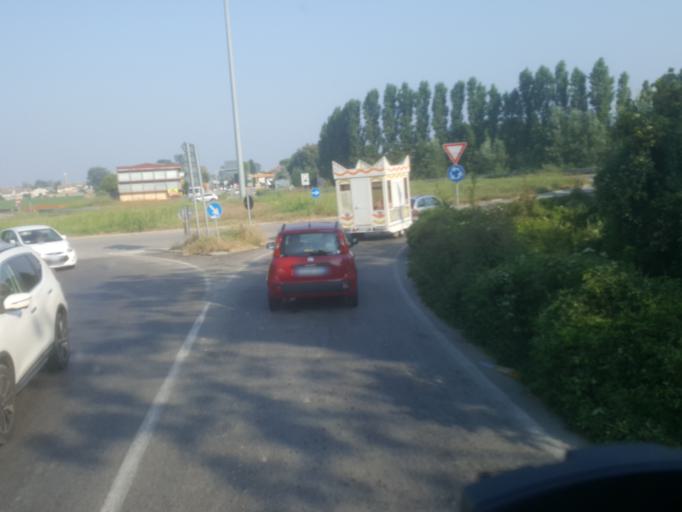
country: IT
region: Emilia-Romagna
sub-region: Provincia di Ravenna
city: Alfonsine
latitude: 44.4965
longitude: 12.0568
